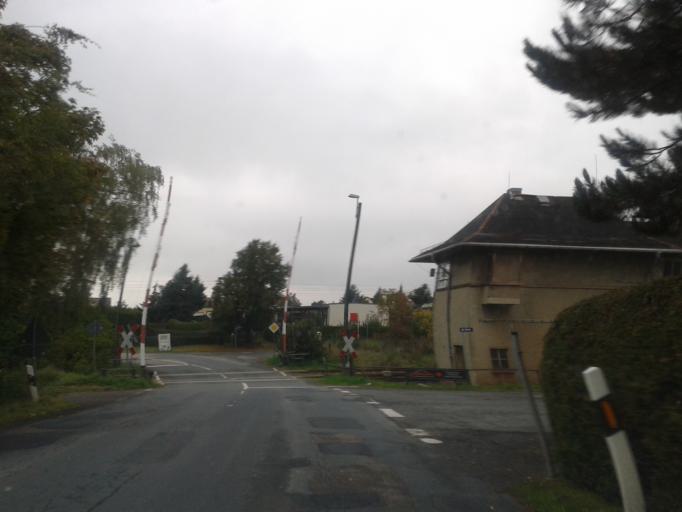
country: DE
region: Saxony
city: Nossen
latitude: 51.0514
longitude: 13.3472
